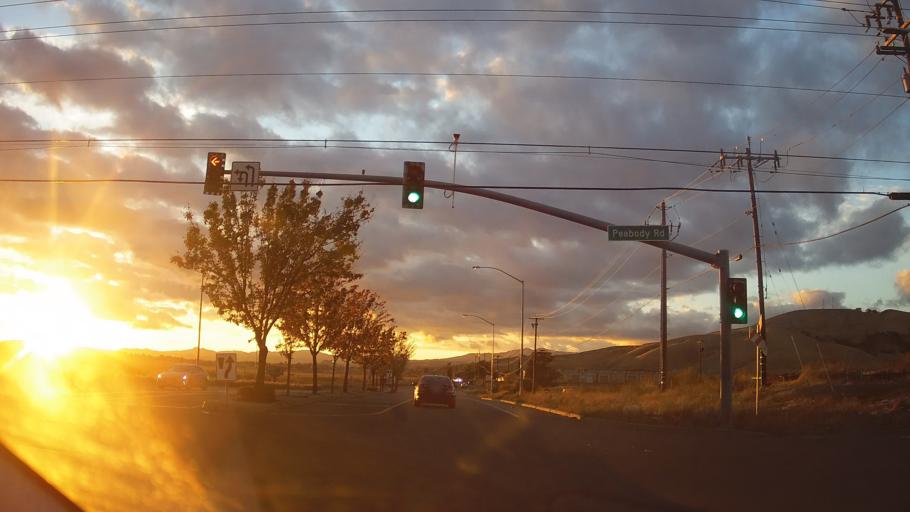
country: US
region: California
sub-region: Solano County
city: Vacaville
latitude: 38.2869
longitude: -121.9696
